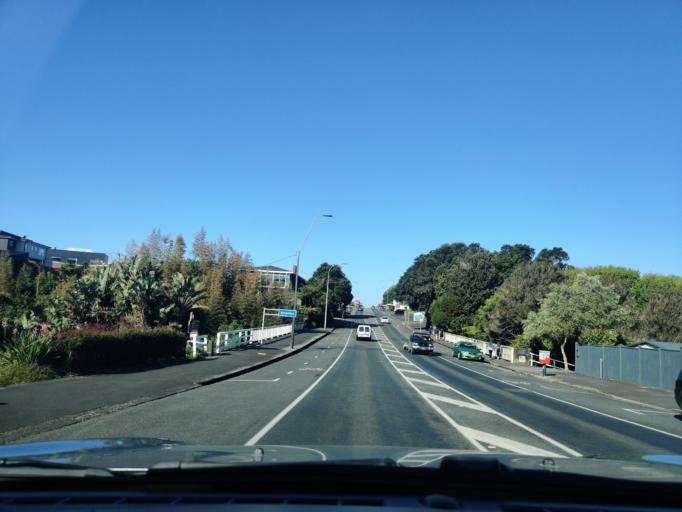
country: NZ
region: Taranaki
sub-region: New Plymouth District
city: New Plymouth
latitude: -39.0526
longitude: 174.0913
